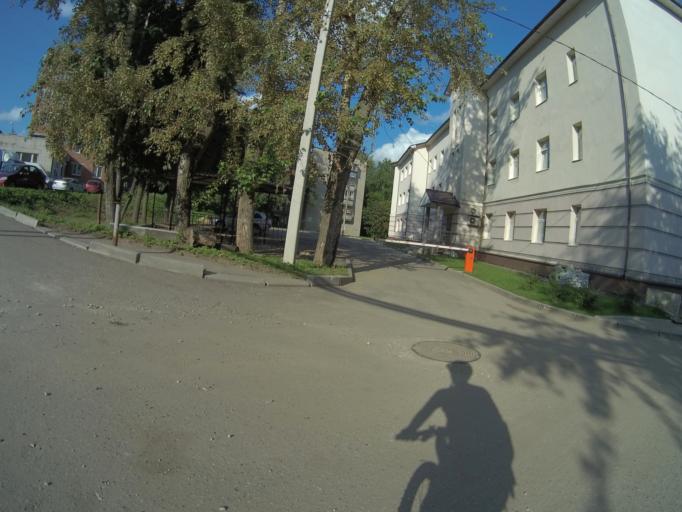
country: RU
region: Vladimir
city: Vladimir
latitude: 56.1418
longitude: 40.3828
